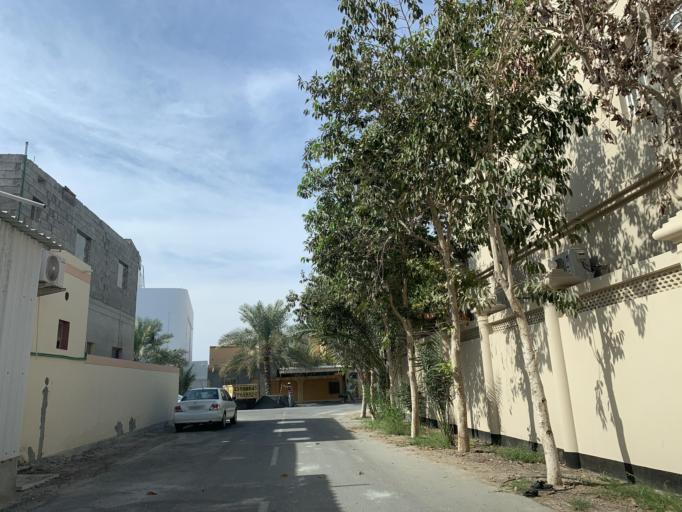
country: BH
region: Central Governorate
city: Madinat Hamad
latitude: 26.1278
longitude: 50.4755
